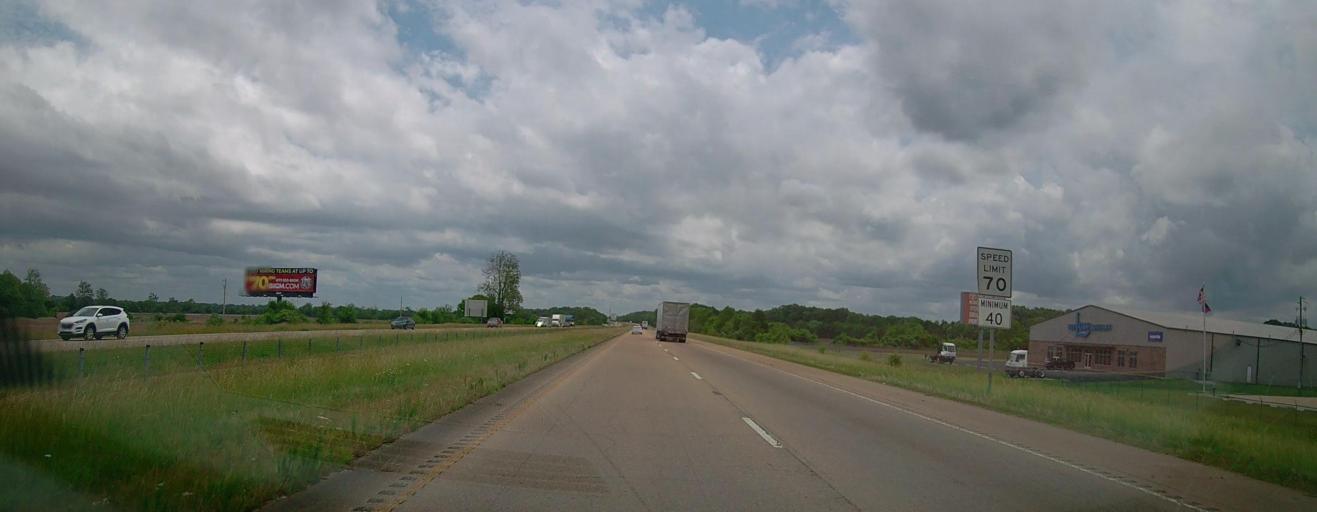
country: US
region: Mississippi
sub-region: Lee County
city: Saltillo
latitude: 34.3458
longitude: -88.8335
